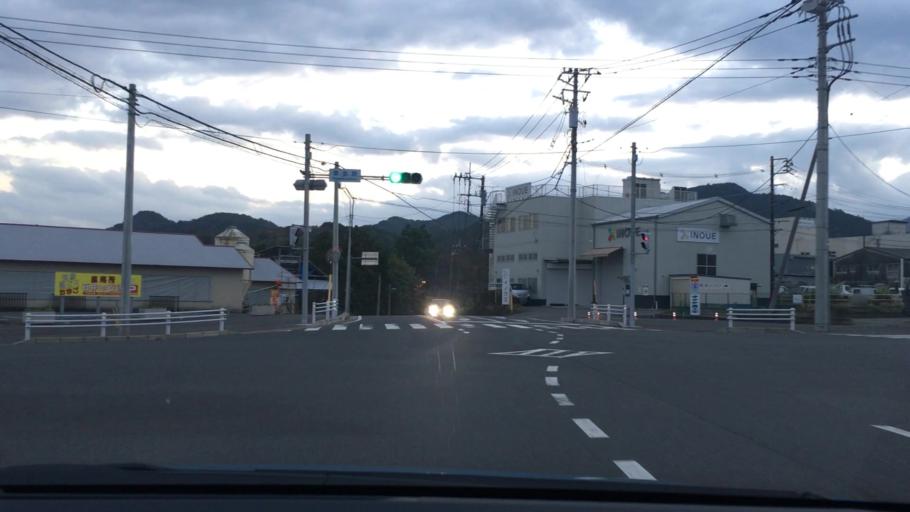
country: JP
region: Tokyo
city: Hachioji
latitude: 35.5745
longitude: 139.2757
